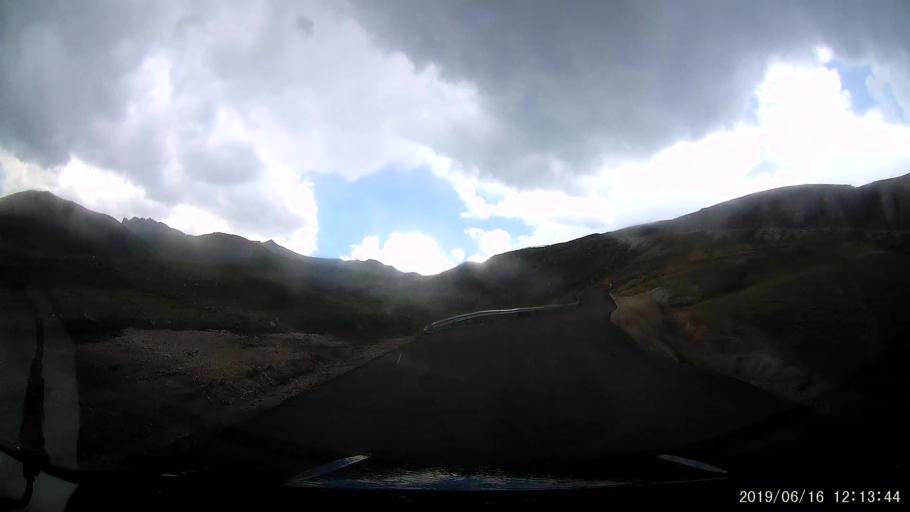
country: TR
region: Agri
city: Dogubayazit
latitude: 39.4472
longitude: 44.2389
